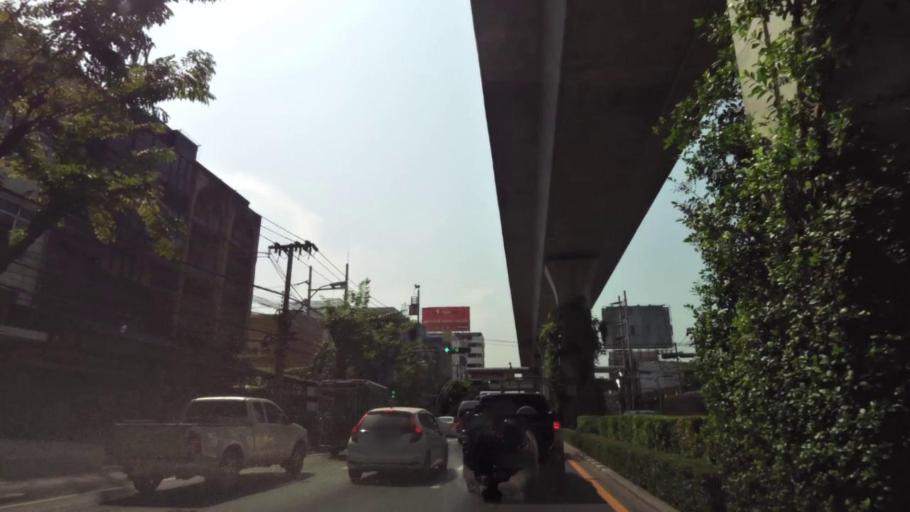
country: TH
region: Bangkok
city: Bang Na
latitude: 13.6593
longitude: 100.6010
